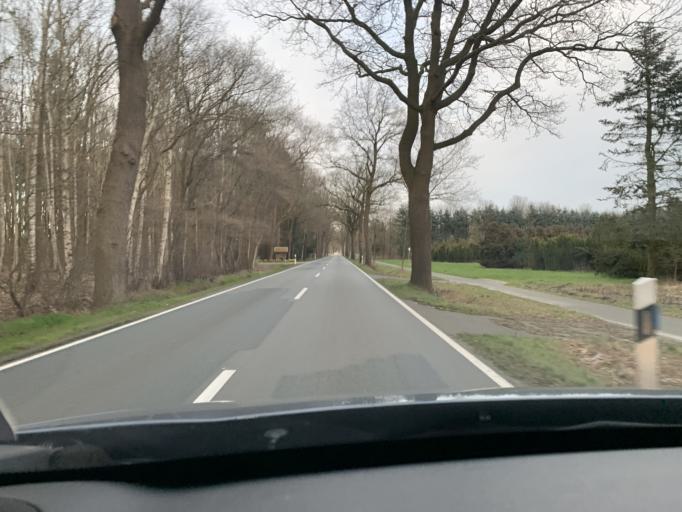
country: DE
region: Lower Saxony
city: Apen
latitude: 53.1793
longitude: 7.8352
